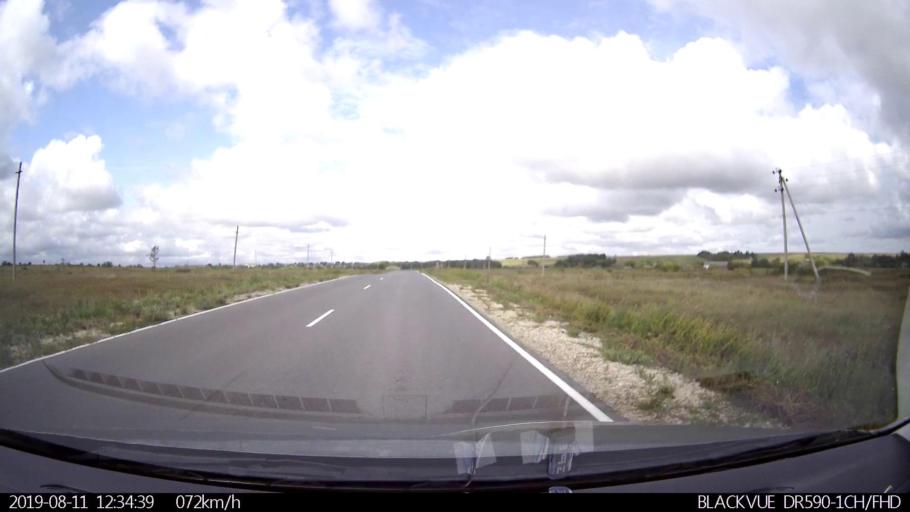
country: RU
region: Ulyanovsk
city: Ignatovka
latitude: 53.8185
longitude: 47.8398
